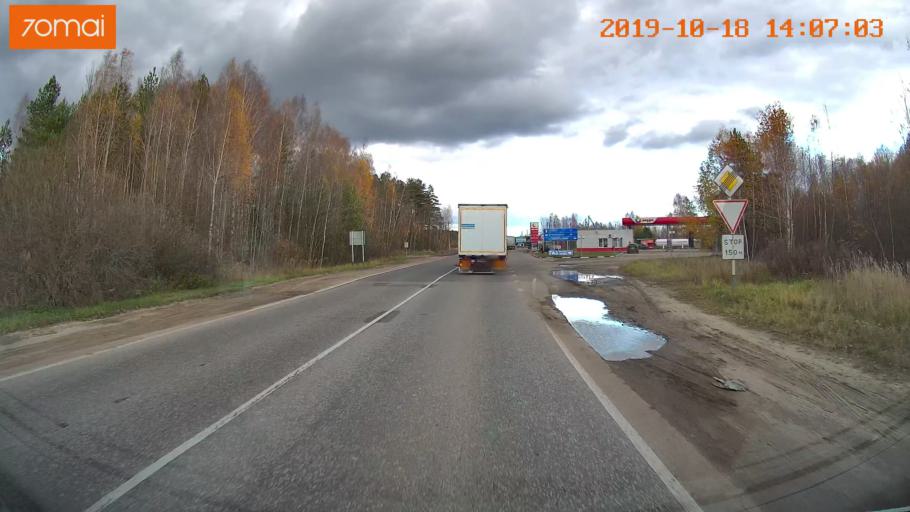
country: RU
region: Rjazan
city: Spas-Klepiki
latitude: 55.1502
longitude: 40.1563
